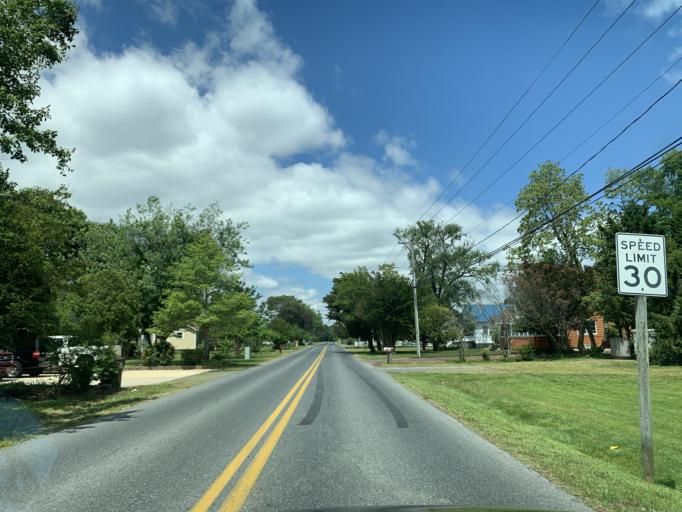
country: US
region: Maryland
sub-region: Worcester County
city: West Ocean City
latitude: 38.3459
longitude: -75.1016
